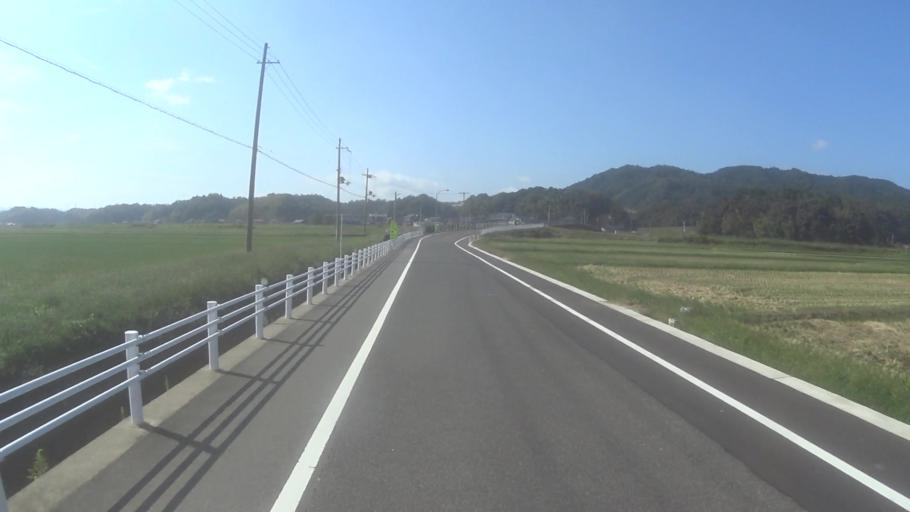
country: JP
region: Kyoto
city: Miyazu
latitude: 35.6808
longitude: 135.0962
